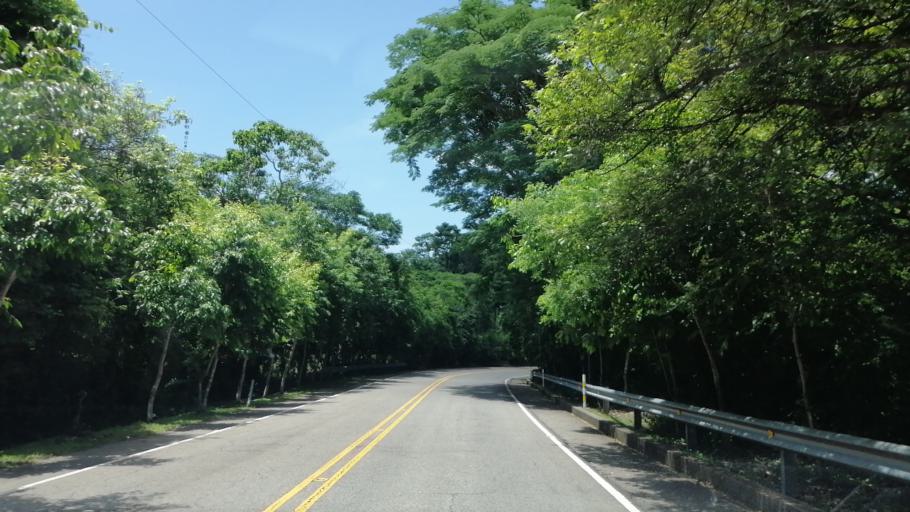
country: SV
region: Chalatenango
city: Nueva Concepcion
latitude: 14.1815
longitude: -89.3223
